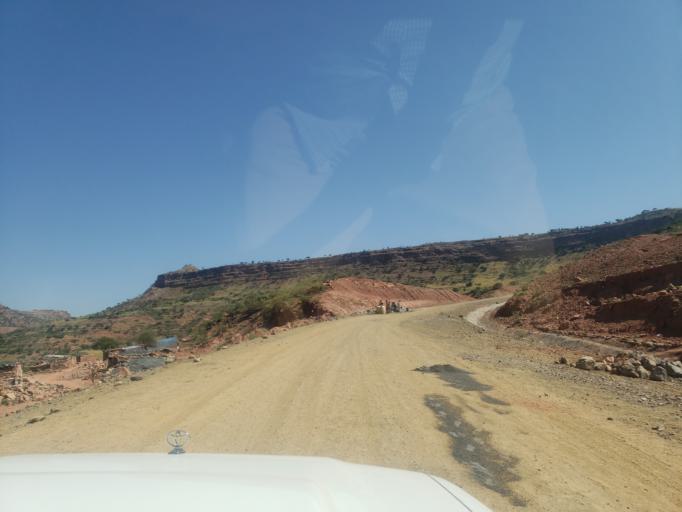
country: ET
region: Tigray
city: Aksum
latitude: 13.5325
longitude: 38.5713
